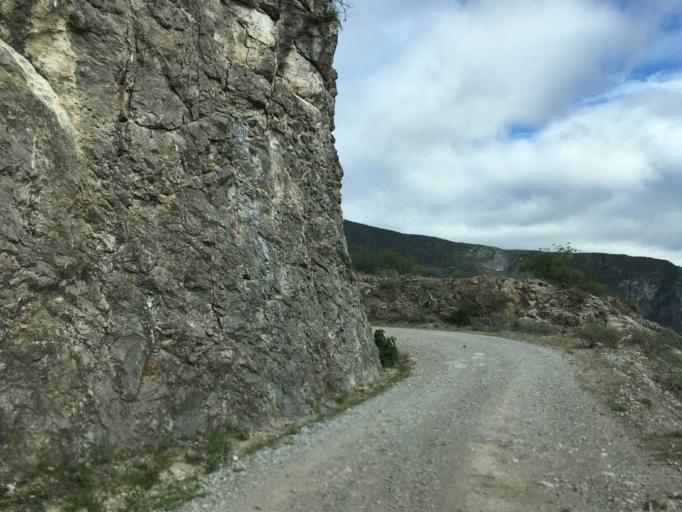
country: MX
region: Hidalgo
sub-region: Metztitlan
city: Fontezuelas
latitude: 20.6410
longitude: -98.9343
